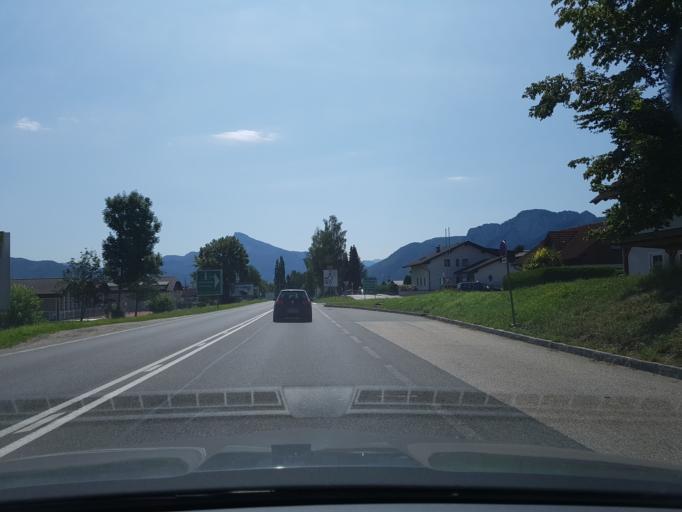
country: AT
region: Upper Austria
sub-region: Politischer Bezirk Vocklabruck
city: Mondsee
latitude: 47.8596
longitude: 13.3406
